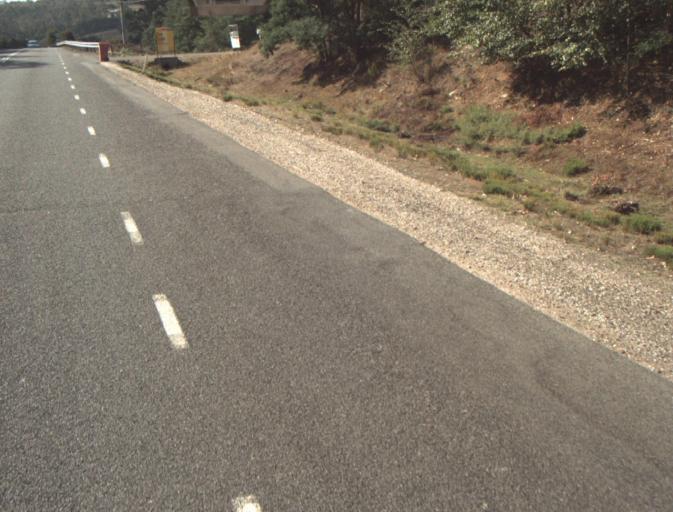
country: AU
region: Tasmania
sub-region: Launceston
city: Mayfield
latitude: -41.2861
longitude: 147.2181
